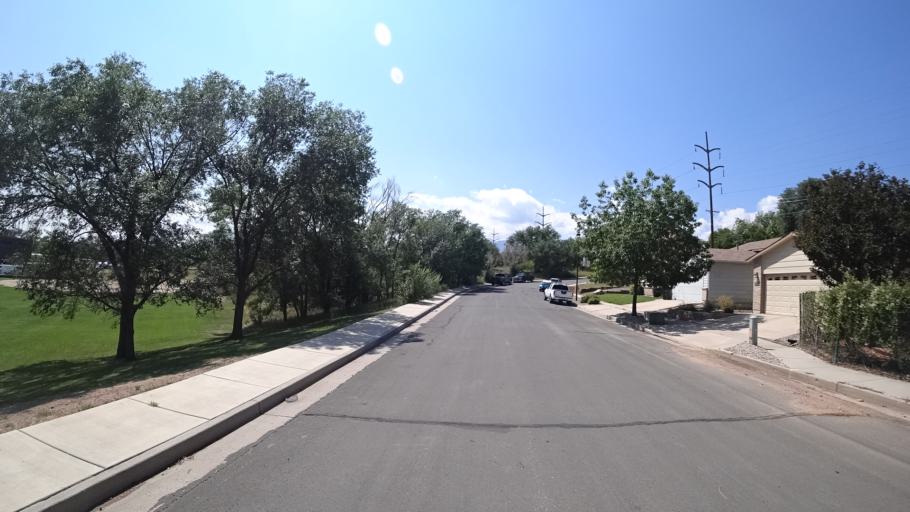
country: US
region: Colorado
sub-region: El Paso County
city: Colorado Springs
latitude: 38.8699
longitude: -104.8380
